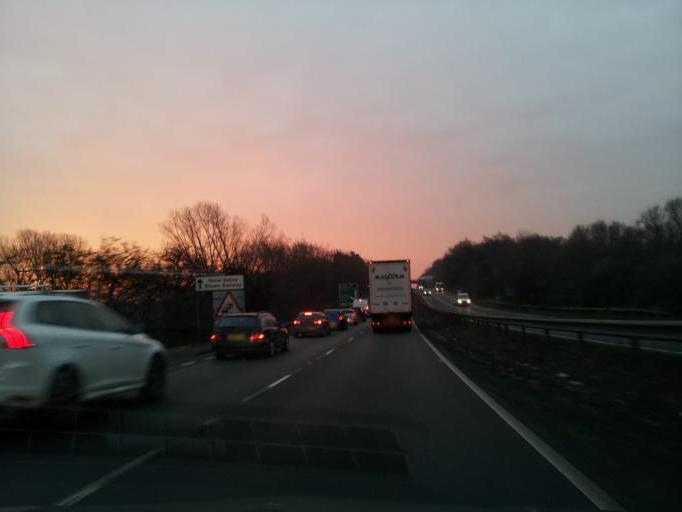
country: GB
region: England
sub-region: Peterborough
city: Thornhaugh
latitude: 52.5892
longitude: -0.4161
